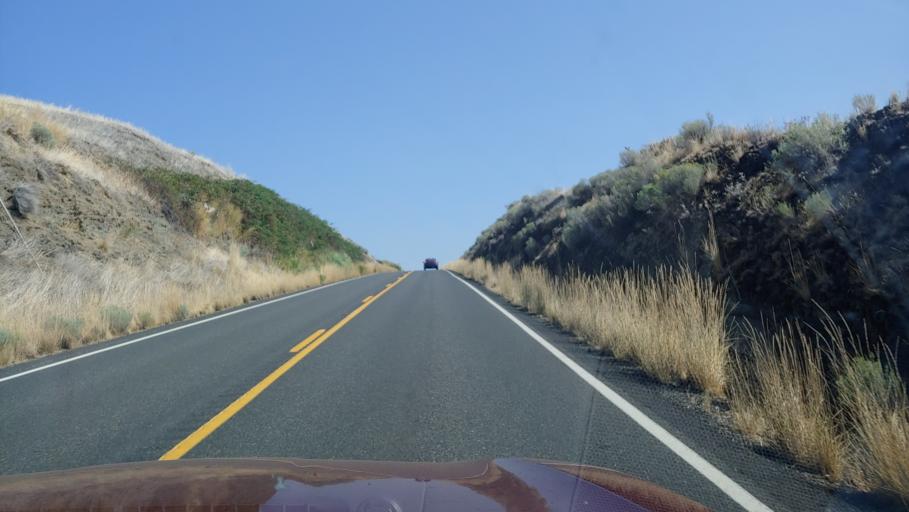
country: US
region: Washington
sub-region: Klickitat County
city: Goldendale
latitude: 45.7007
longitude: -120.8032
